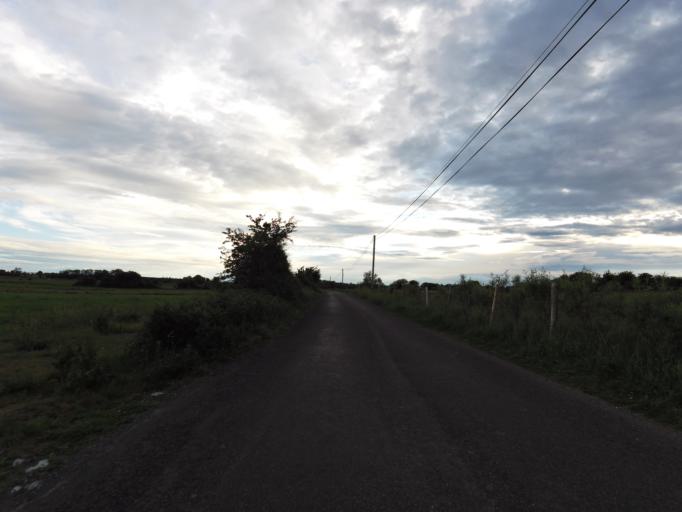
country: IE
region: Connaught
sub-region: County Galway
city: Athenry
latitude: 53.2902
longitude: -8.7060
